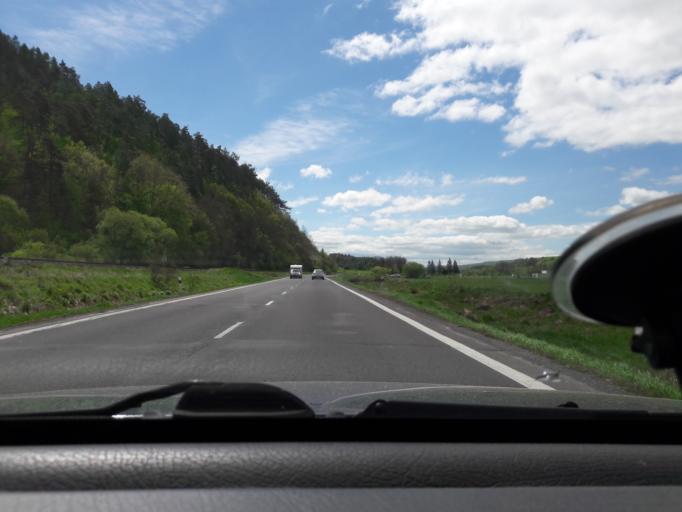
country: SK
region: Banskobystricky
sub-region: Okres Banska Bystrica
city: Zvolen
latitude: 48.5112
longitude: 19.0984
